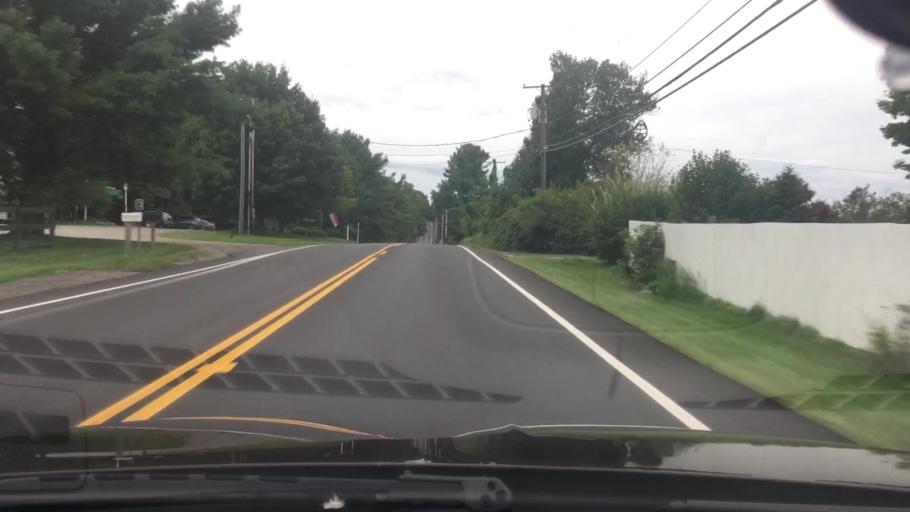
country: US
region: New York
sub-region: Dutchess County
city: Millbrook
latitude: 41.8219
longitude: -73.6237
